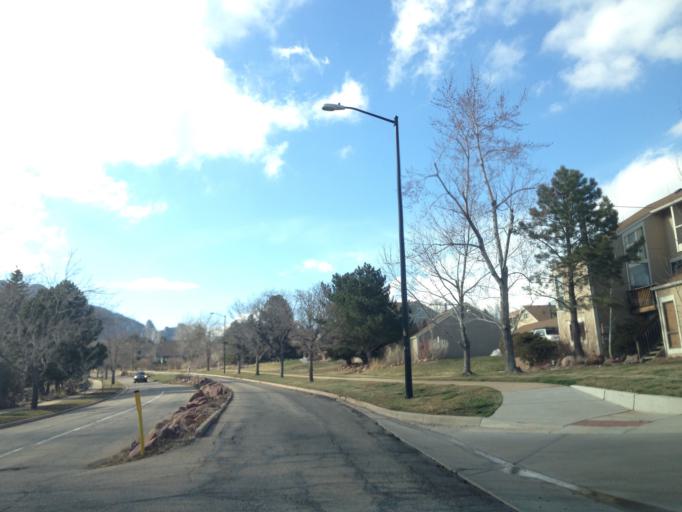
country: US
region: Colorado
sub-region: Boulder County
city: Boulder
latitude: 39.9658
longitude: -105.2549
